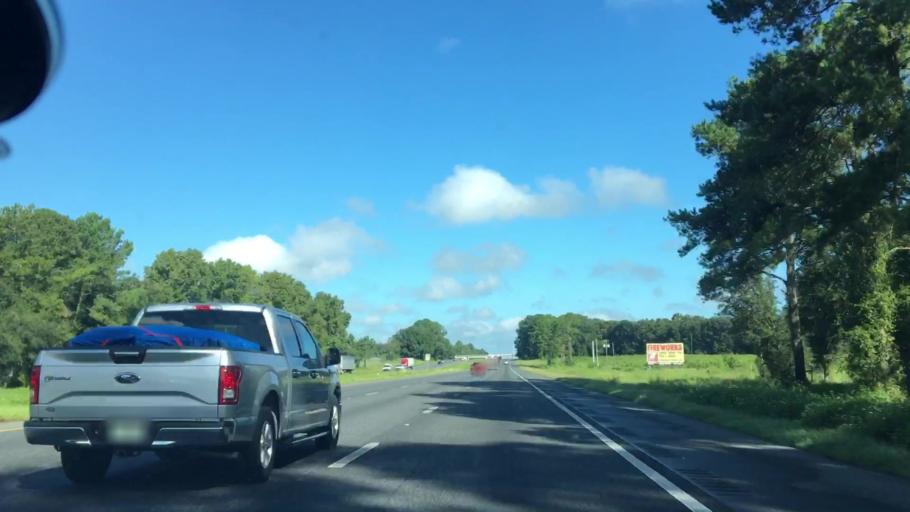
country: US
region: Florida
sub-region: Suwannee County
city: Wellborn
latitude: 30.2869
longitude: -82.7692
